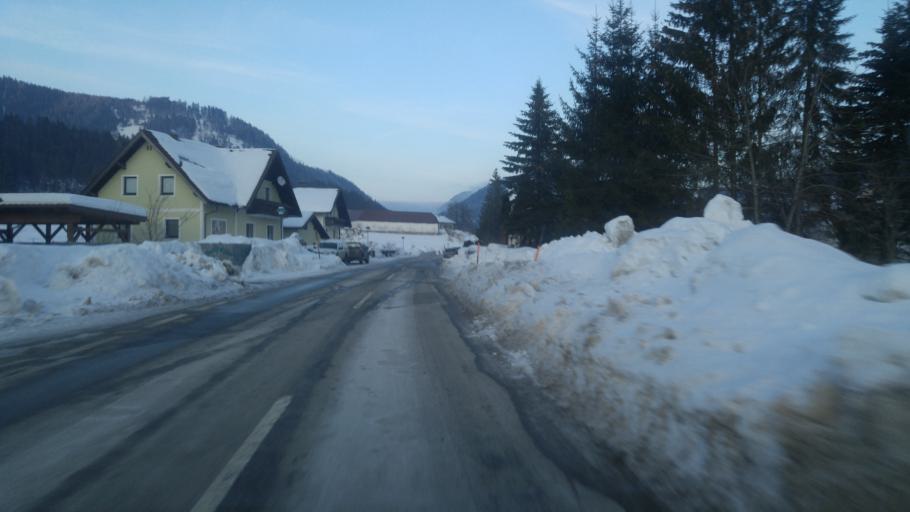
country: AT
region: Lower Austria
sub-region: Politischer Bezirk Wiener Neustadt
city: Rohr im Gebirge
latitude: 47.8898
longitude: 15.7192
